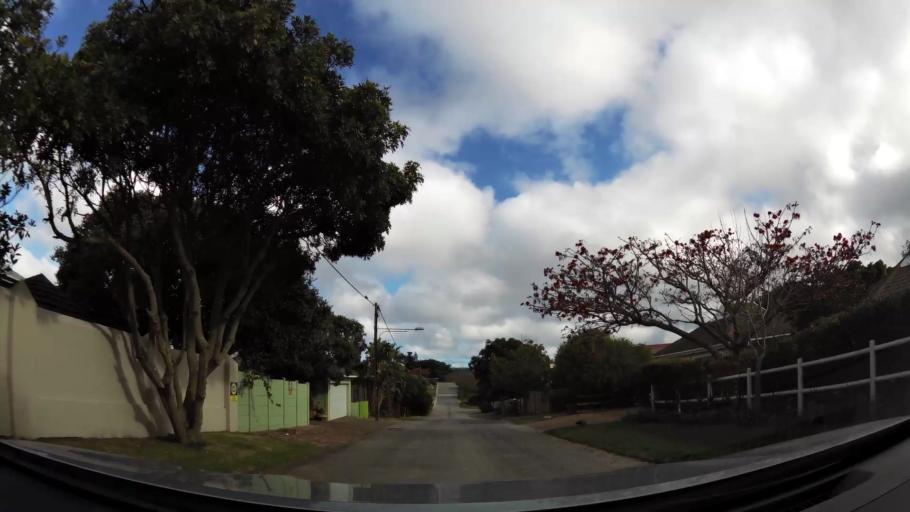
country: ZA
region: Western Cape
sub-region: Eden District Municipality
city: Plettenberg Bay
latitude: -34.0691
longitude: 23.3704
